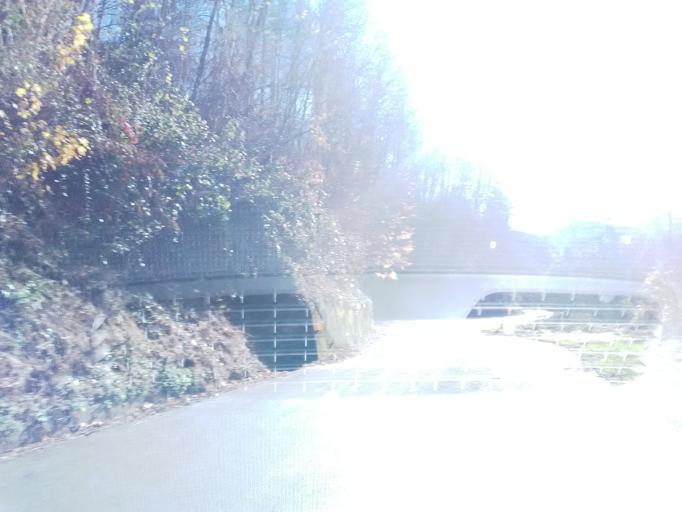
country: IT
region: Piedmont
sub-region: Provincia di Biella
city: Ailoche
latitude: 45.6954
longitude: 8.2253
